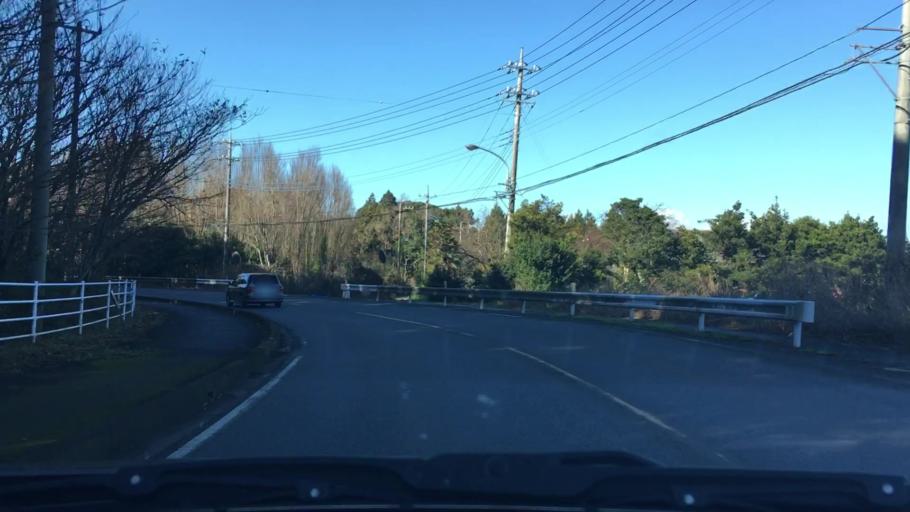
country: JP
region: Chiba
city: Sawara
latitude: 35.8390
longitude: 140.5447
